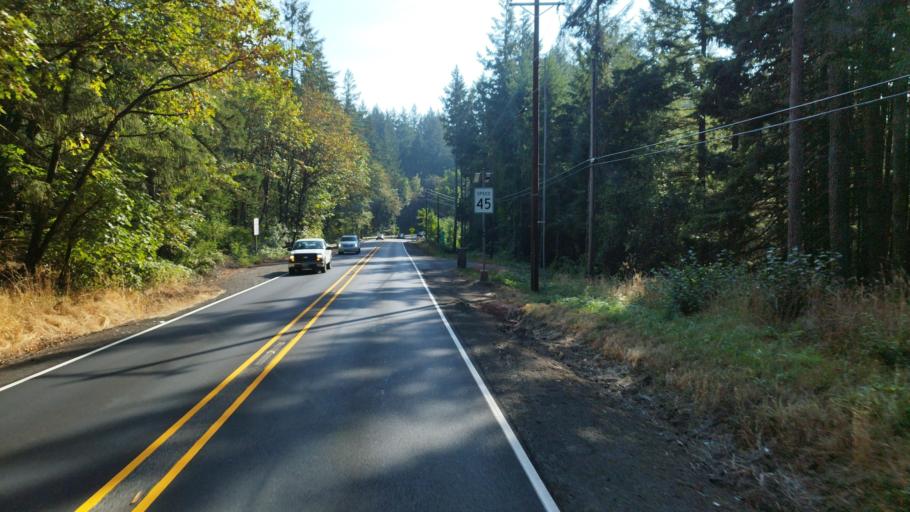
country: US
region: Oregon
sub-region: Washington County
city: Bethany
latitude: 45.6022
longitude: -122.8610
